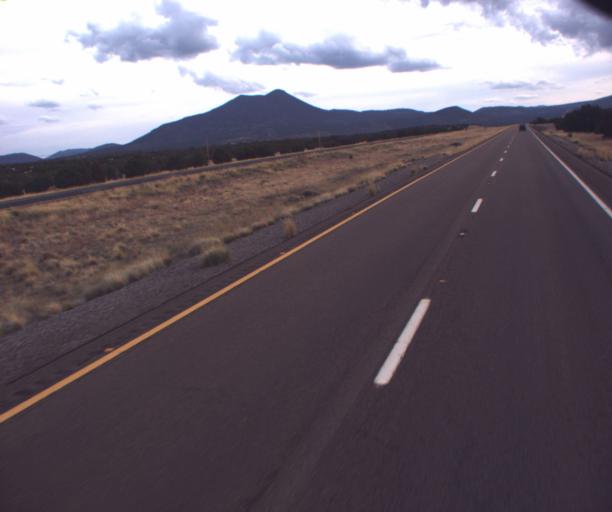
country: US
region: Arizona
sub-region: Coconino County
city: Flagstaff
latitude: 35.4793
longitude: -111.5570
